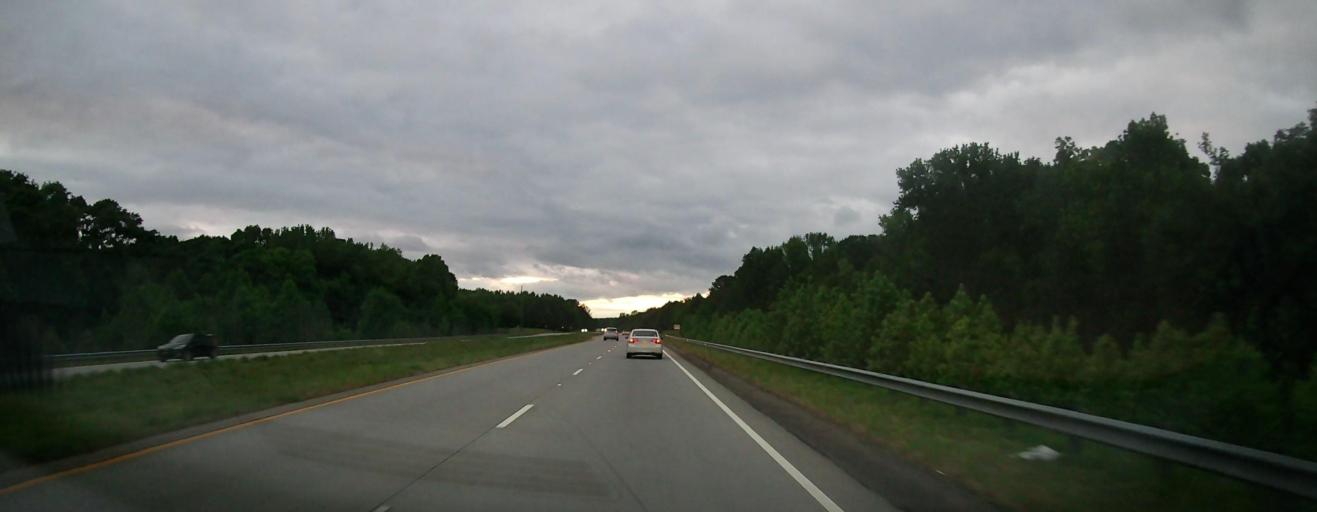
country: US
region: Georgia
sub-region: Jackson County
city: Arcade
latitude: 34.0781
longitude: -83.5741
